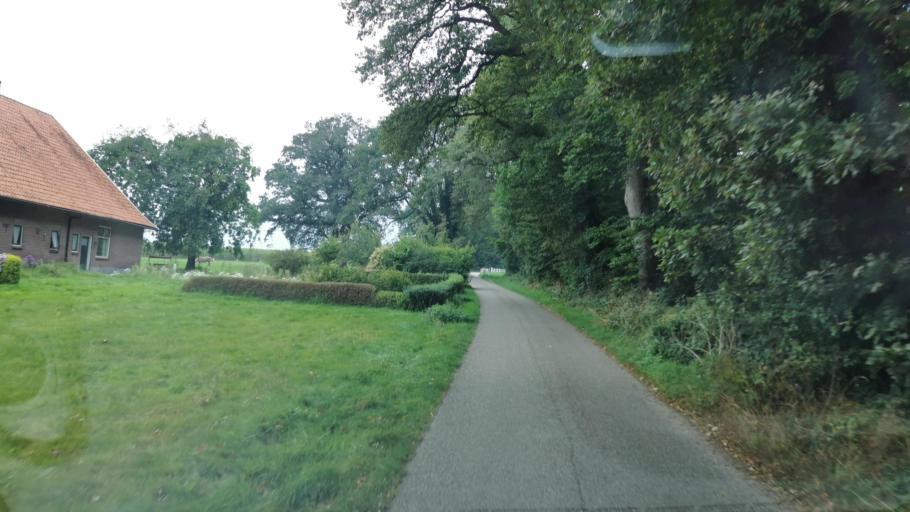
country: NL
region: Overijssel
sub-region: Gemeente Oldenzaal
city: Oldenzaal
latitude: 52.3134
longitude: 6.9681
